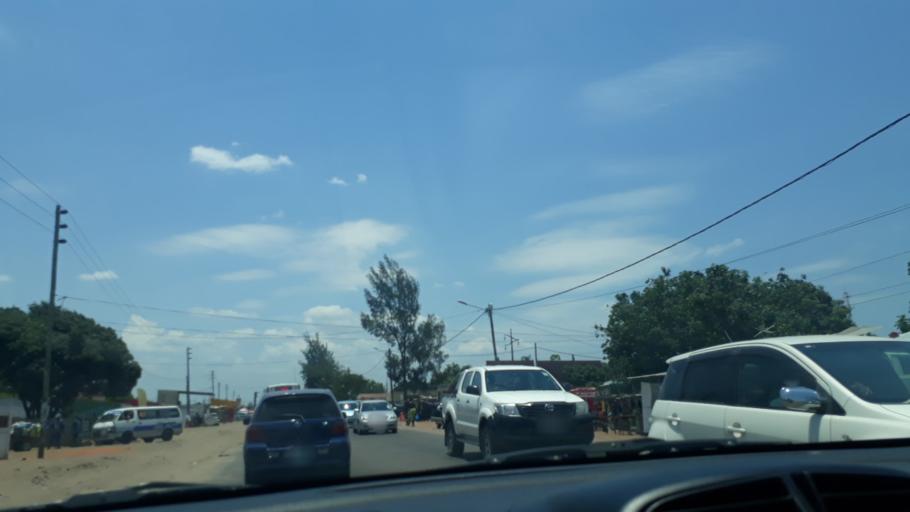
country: MZ
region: Maputo City
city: Maputo
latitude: -25.8891
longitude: 32.6034
